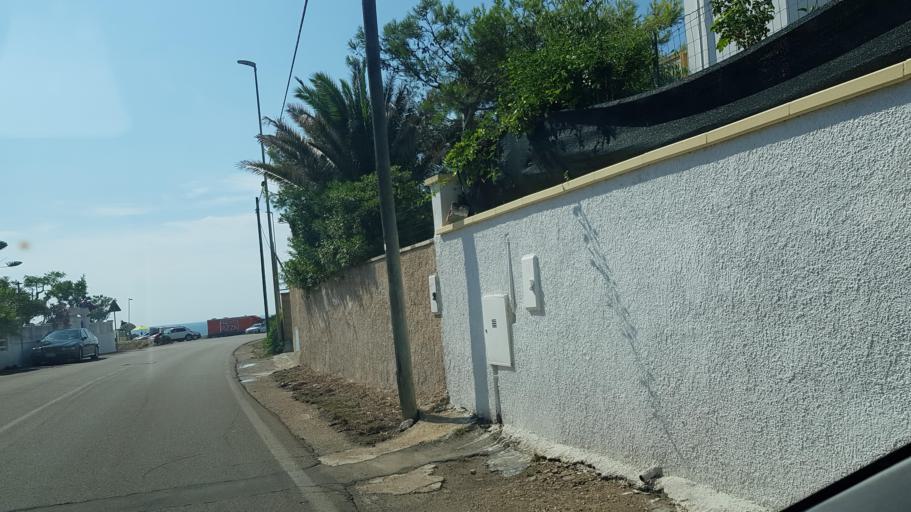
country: IT
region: Apulia
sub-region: Provincia di Lecce
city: Leuca
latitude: 39.7926
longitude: 18.3447
